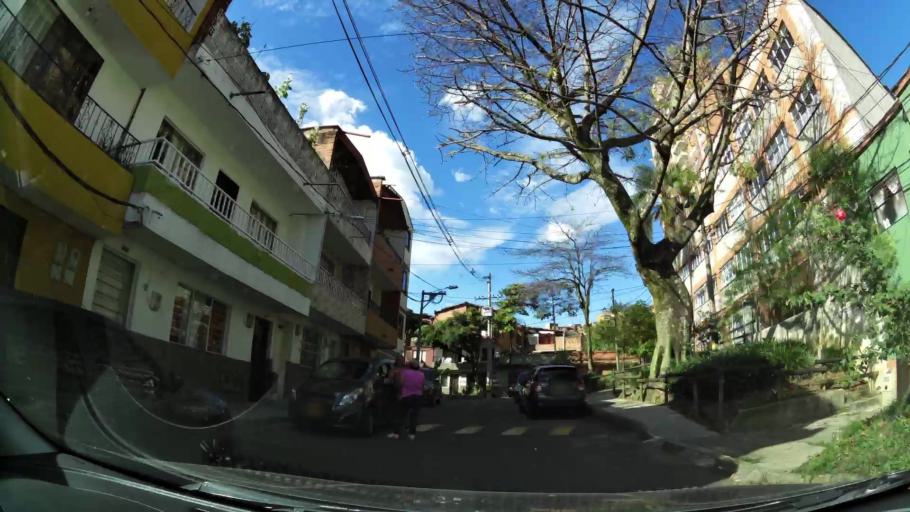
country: CO
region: Antioquia
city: Envigado
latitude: 6.1677
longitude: -75.5787
